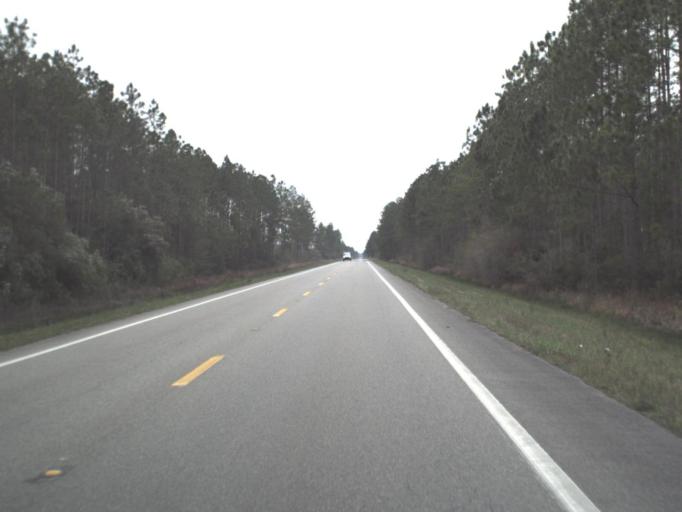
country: US
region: Florida
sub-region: Gulf County
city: Port Saint Joe
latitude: 29.9270
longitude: -85.1954
